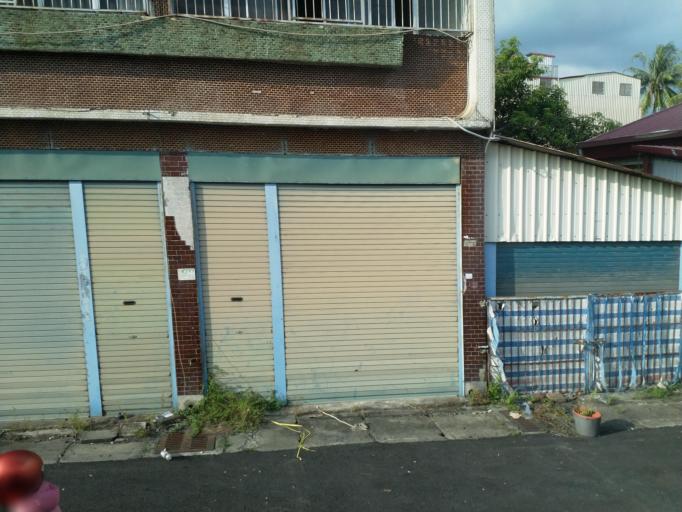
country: TW
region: Taiwan
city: Yujing
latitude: 22.9019
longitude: 120.5387
